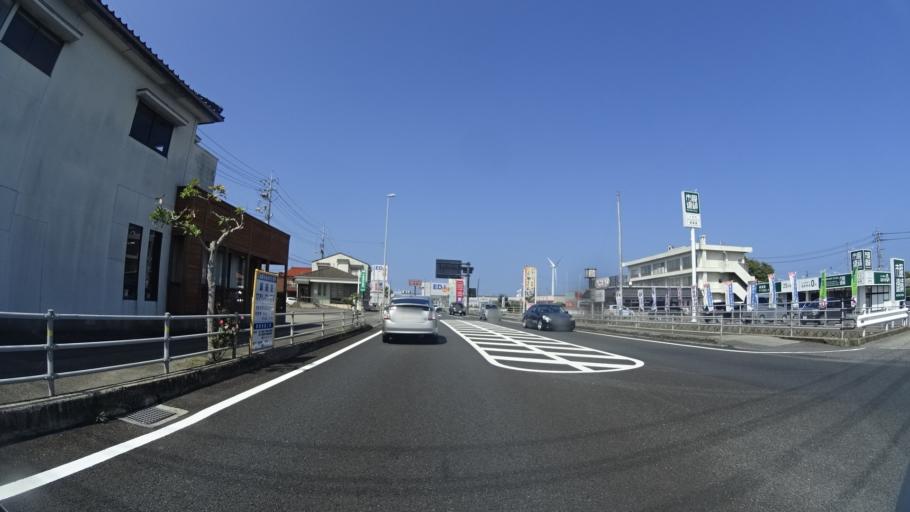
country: JP
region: Shimane
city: Masuda
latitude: 34.6887
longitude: 131.8234
